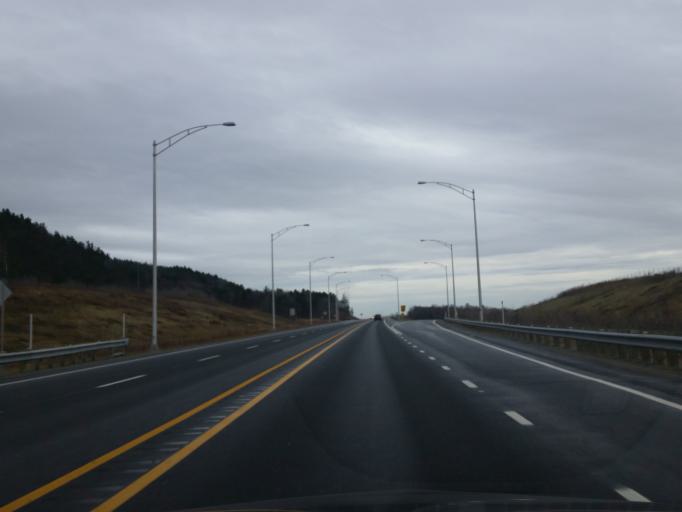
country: CA
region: Quebec
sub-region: Outaouais
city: Papineauville
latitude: 45.6611
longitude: -74.8760
